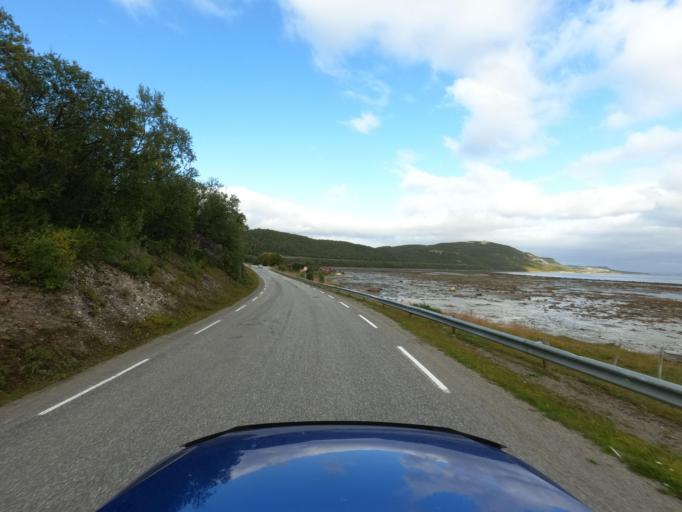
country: NO
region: Finnmark Fylke
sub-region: Porsanger
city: Lakselv
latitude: 70.2260
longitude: 24.9421
